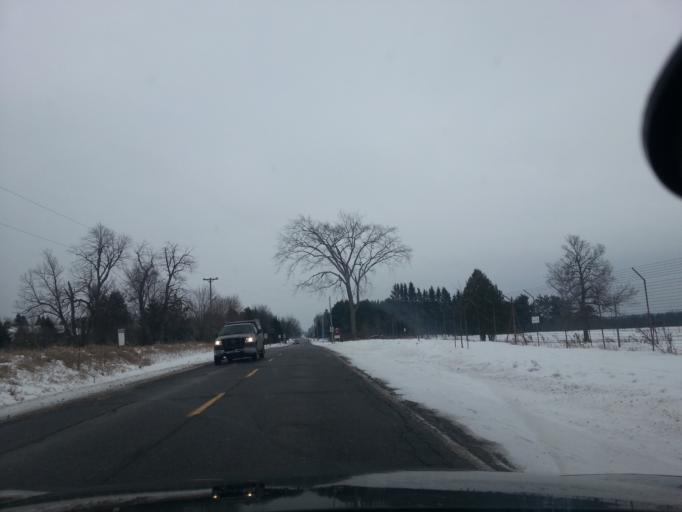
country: CA
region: Ontario
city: Bells Corners
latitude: 45.3536
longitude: -76.0470
